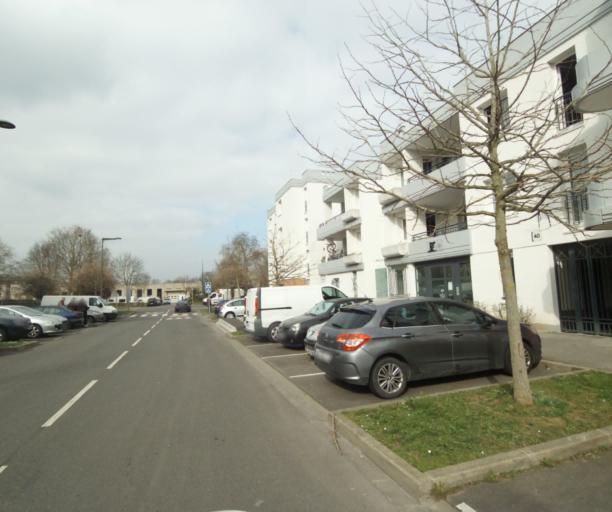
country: FR
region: Ile-de-France
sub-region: Departement du Val-d'Oise
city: Vaureal
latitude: 49.0503
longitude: 2.0400
